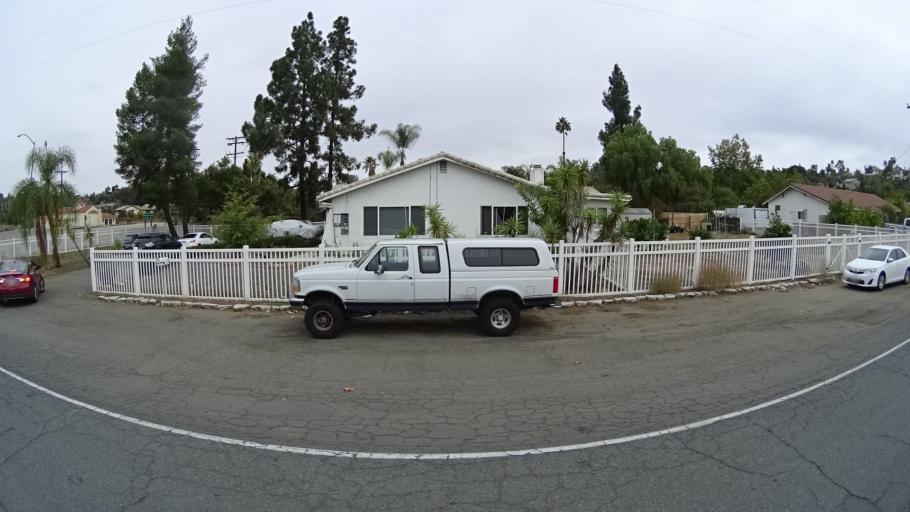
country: US
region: California
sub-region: San Diego County
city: Rancho San Diego
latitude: 32.7702
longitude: -116.9273
